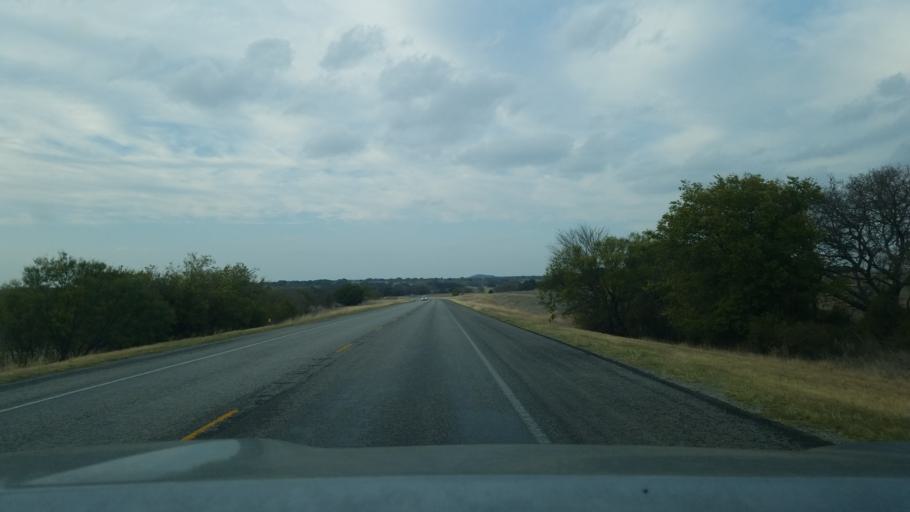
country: US
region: Texas
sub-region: Mills County
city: Goldthwaite
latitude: 31.5066
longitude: -98.5816
